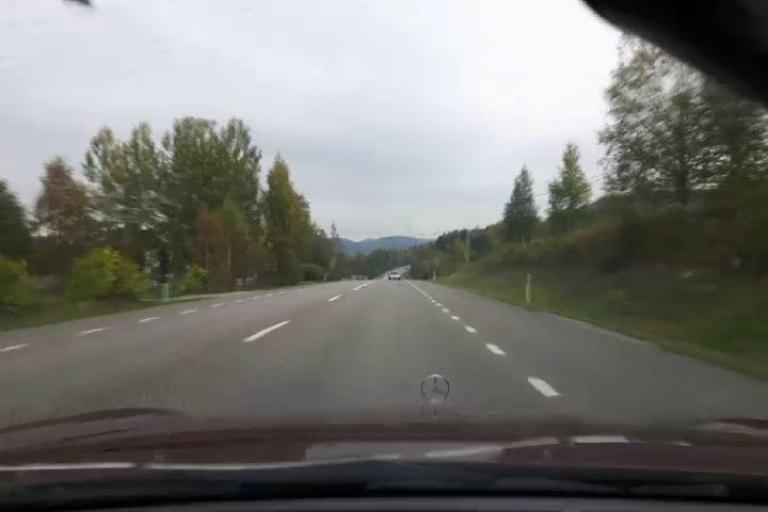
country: SE
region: Vaesternorrland
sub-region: Kramfors Kommun
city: Nordingra
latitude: 63.0170
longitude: 18.2940
